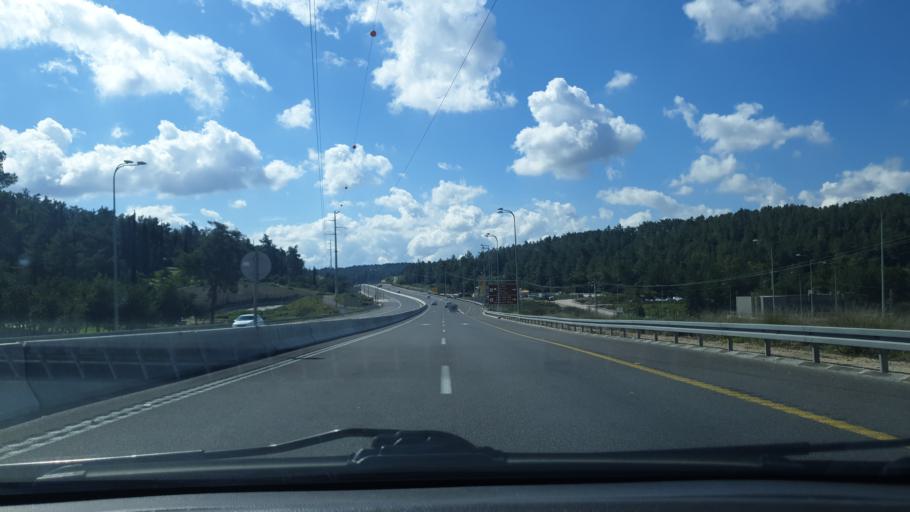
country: IL
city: Mevo horon
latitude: 31.8111
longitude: 35.0201
